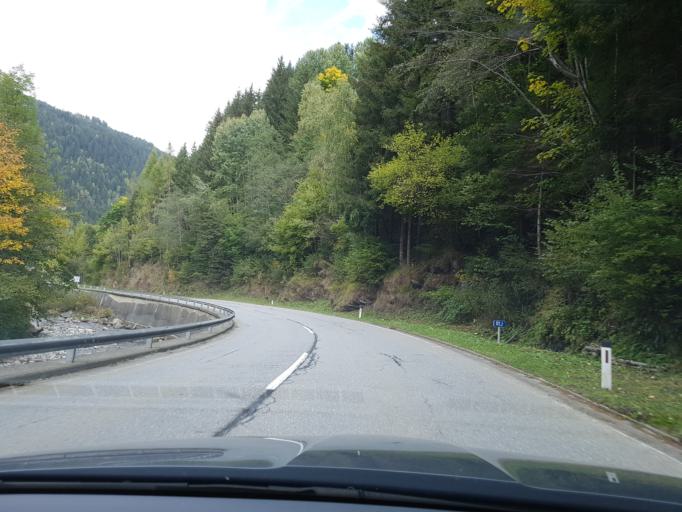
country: AT
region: Styria
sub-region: Politischer Bezirk Murau
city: Stadl an der Mur
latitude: 47.0670
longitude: 13.9148
